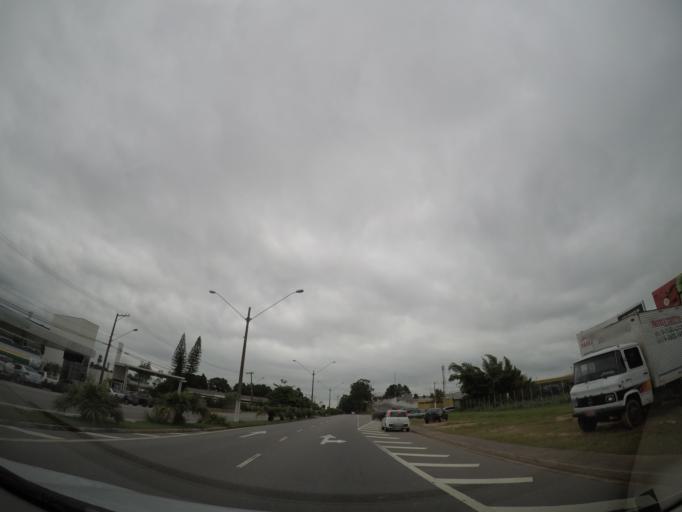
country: BR
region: Sao Paulo
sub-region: Jundiai
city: Jundiai
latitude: -23.1425
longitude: -46.9157
